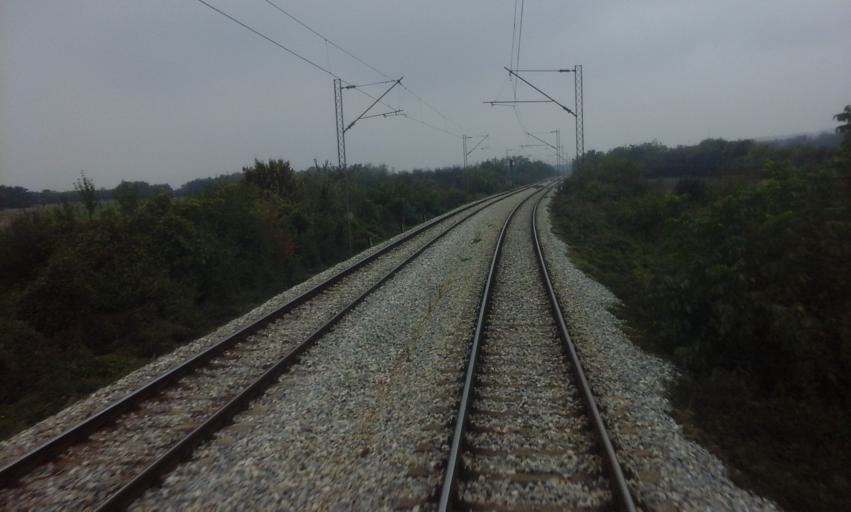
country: RS
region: Central Serbia
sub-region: Sumadijski Okrug
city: Lapovo
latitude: 44.2180
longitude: 21.0948
